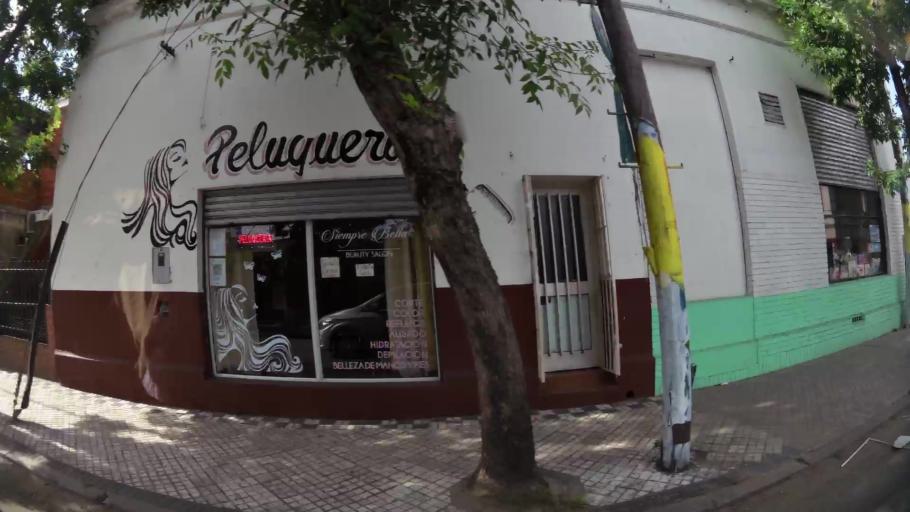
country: AR
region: Santa Fe
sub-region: Departamento de Rosario
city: Rosario
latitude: -32.9197
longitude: -60.6964
